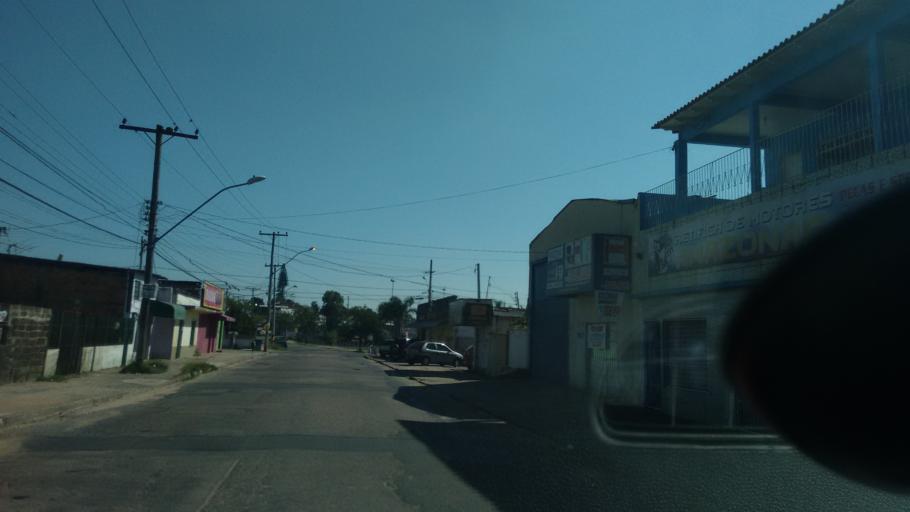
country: BR
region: Rio Grande do Sul
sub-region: Viamao
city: Viamao
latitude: -30.0575
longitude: -51.1007
